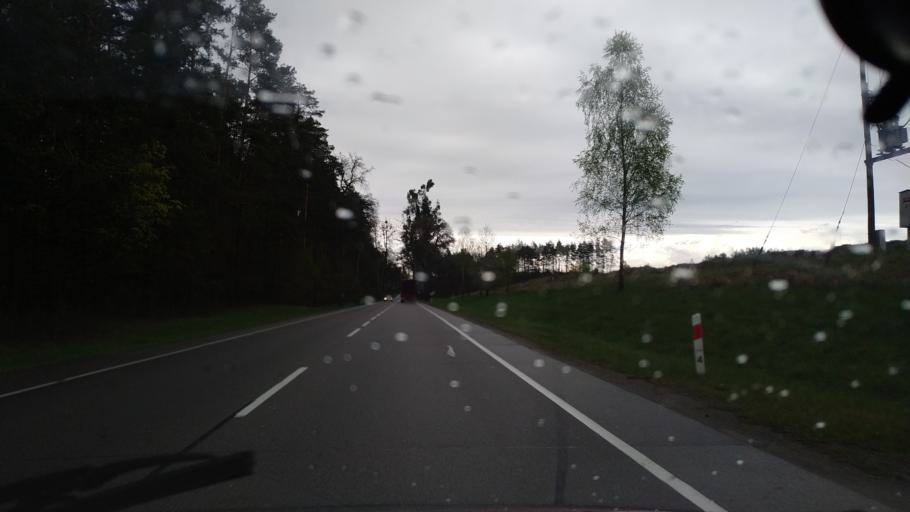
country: PL
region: Pomeranian Voivodeship
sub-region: Powiat starogardzki
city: Kaliska
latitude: 53.8821
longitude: 18.1922
